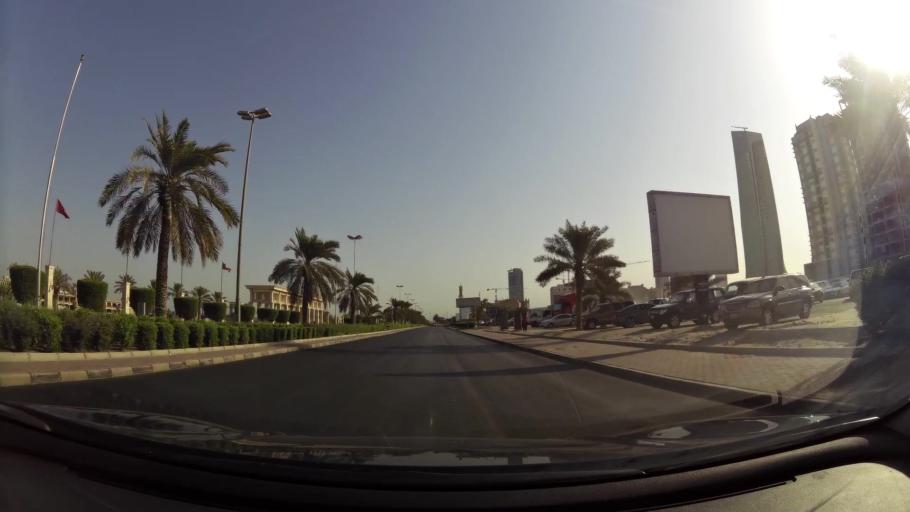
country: KW
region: Al Asimah
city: Kuwait City
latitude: 29.3866
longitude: 47.9822
